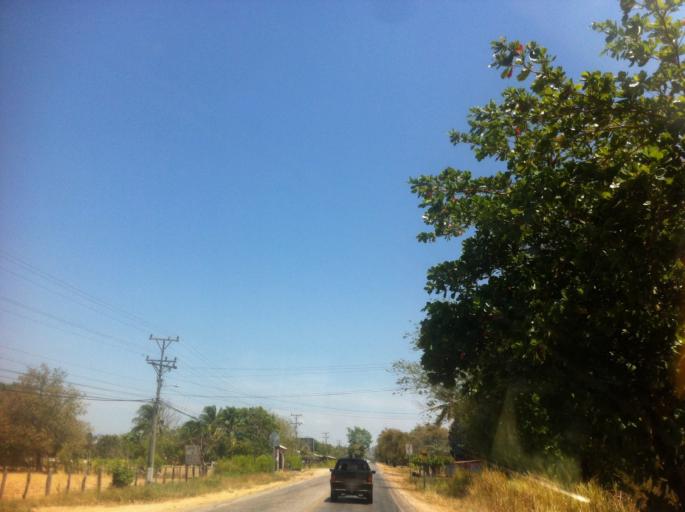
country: CR
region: Guanacaste
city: Santa Cruz
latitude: 10.2874
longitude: -85.5881
